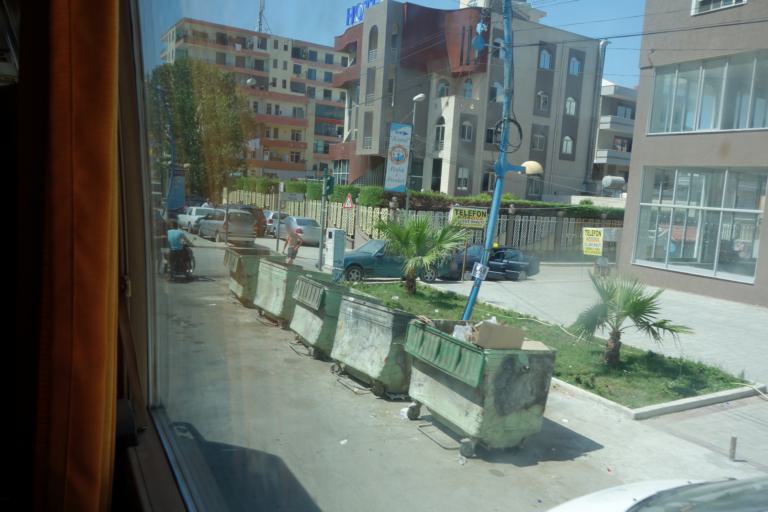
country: AL
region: Durres
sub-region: Rrethi i Durresit
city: Rrashbull
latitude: 41.3125
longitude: 19.4800
